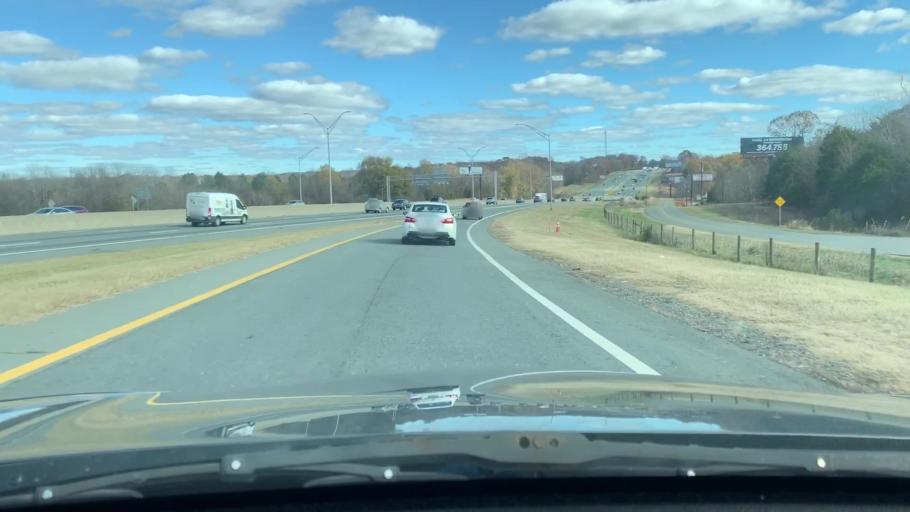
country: US
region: North Carolina
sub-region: Alamance County
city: Haw River
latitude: 36.0684
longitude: -79.3508
